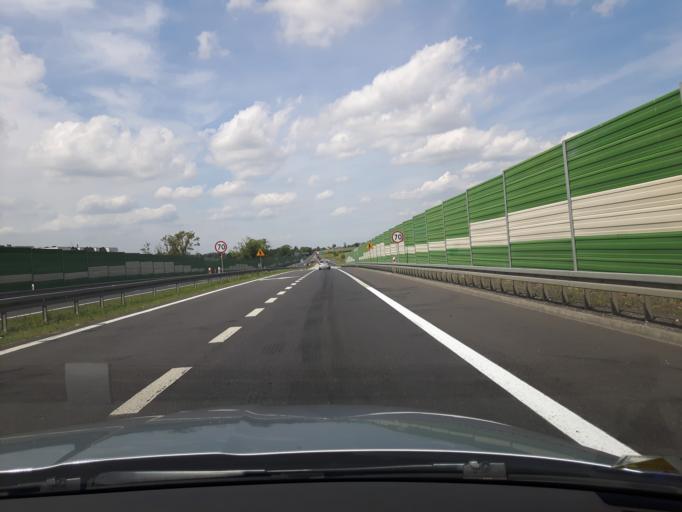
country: PL
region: Masovian Voivodeship
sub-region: Powiat plonski
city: Plonsk
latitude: 52.6323
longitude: 20.3822
